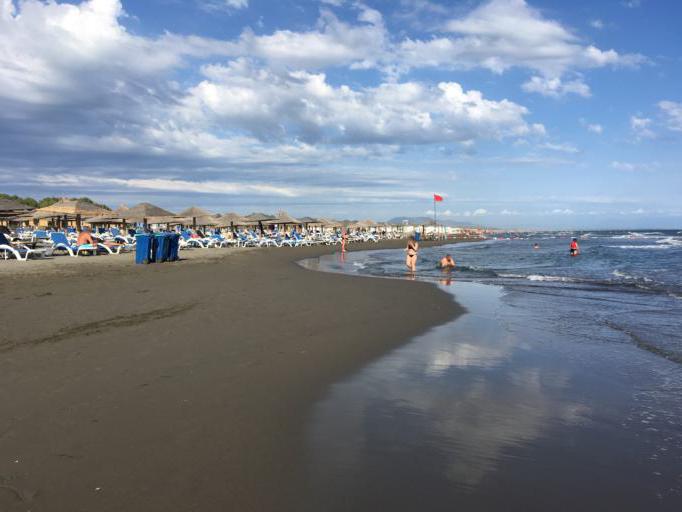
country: ME
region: Ulcinj
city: Ulcinj
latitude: 41.9056
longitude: 19.2541
